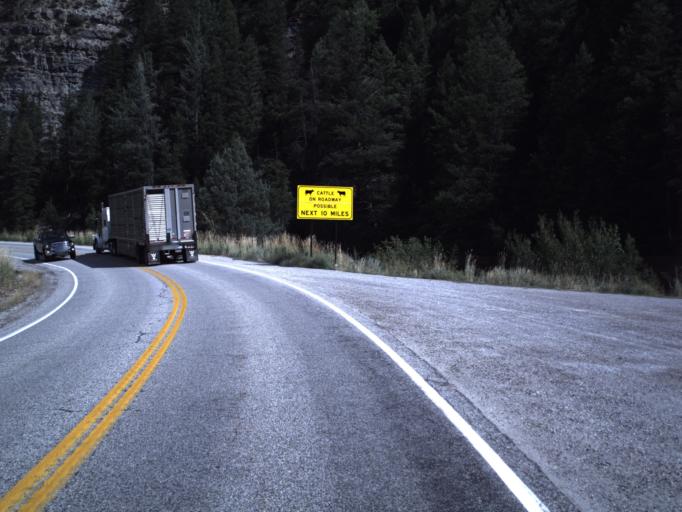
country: US
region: Utah
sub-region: Cache County
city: North Logan
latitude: 41.8326
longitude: -111.5950
